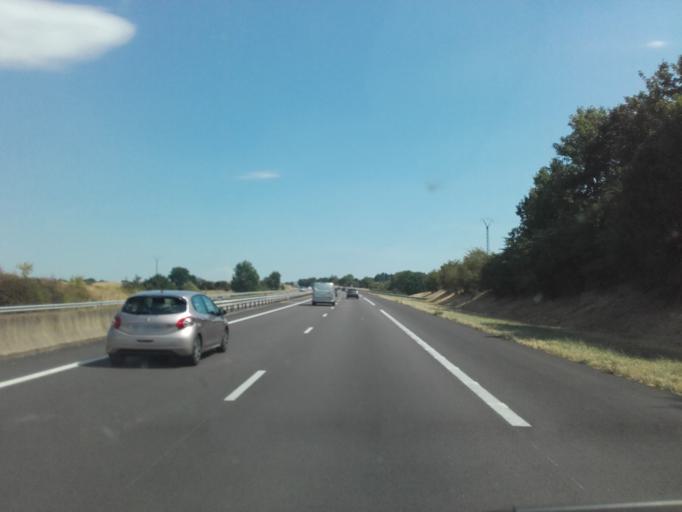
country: FR
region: Bourgogne
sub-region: Departement de la Cote-d'Or
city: Semur-en-Auxois
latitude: 47.3830
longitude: 4.3737
